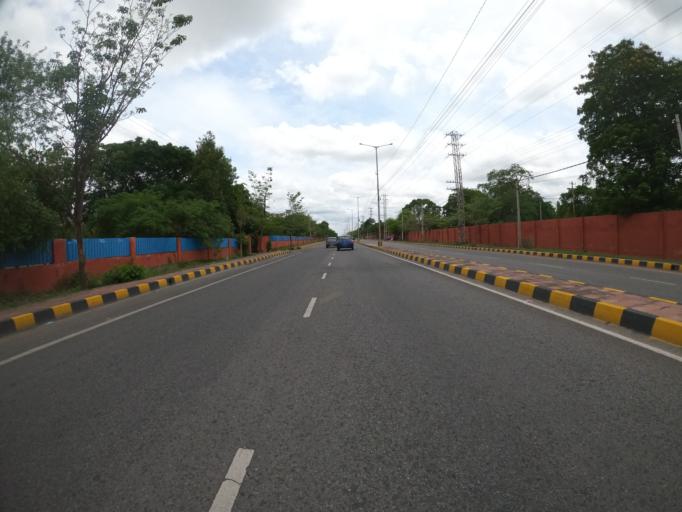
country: IN
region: Telangana
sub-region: Hyderabad
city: Hyderabad
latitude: 17.3763
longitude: 78.3904
